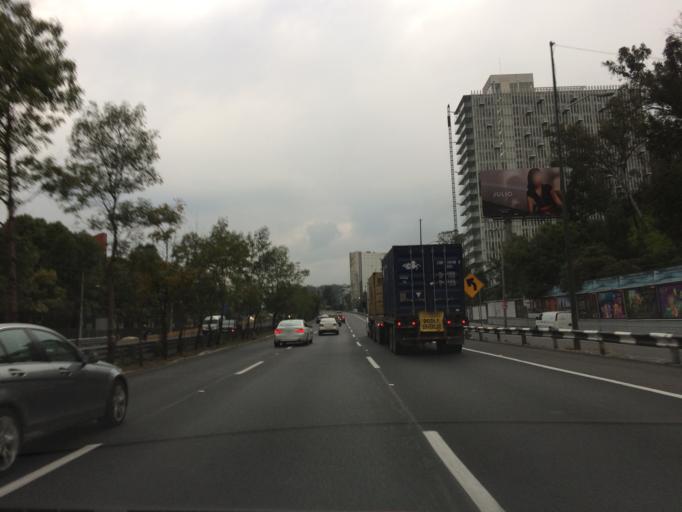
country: MX
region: Mexico City
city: Col. Bosques de las Lomas
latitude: 19.3774
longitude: -99.2569
